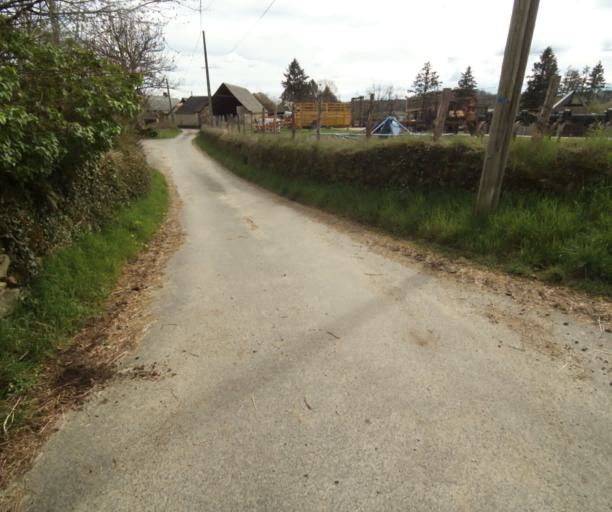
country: FR
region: Limousin
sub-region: Departement de la Correze
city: Argentat
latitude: 45.1812
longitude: 1.9222
